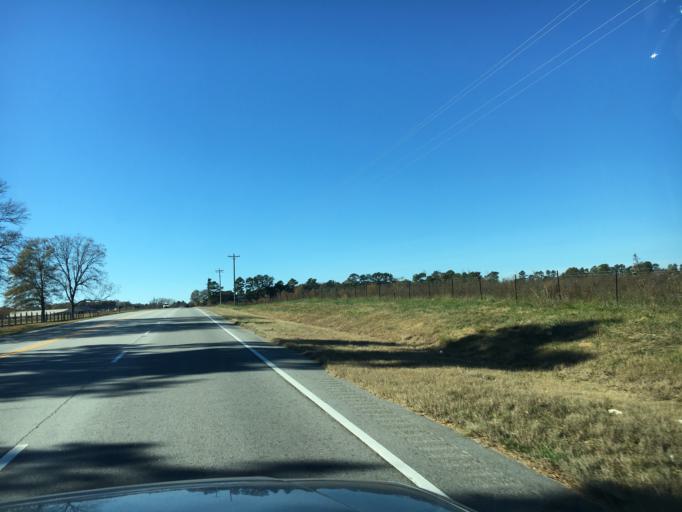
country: US
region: Georgia
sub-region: Hart County
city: Royston
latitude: 34.2936
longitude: -83.0319
